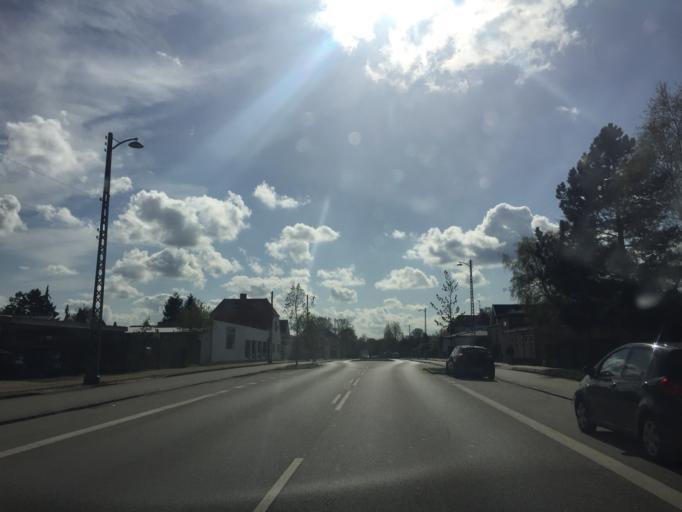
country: DK
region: Capital Region
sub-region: Herlev Kommune
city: Herlev
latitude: 55.7084
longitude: 12.4606
